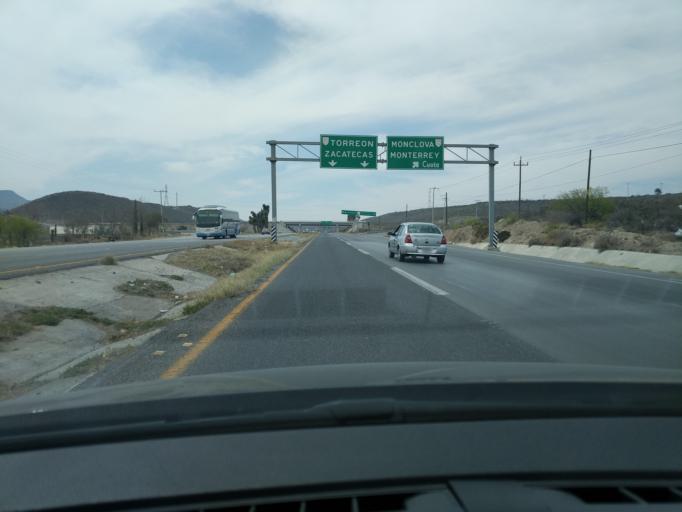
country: MX
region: Coahuila
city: Saltillo
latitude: 25.4534
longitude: -101.0604
